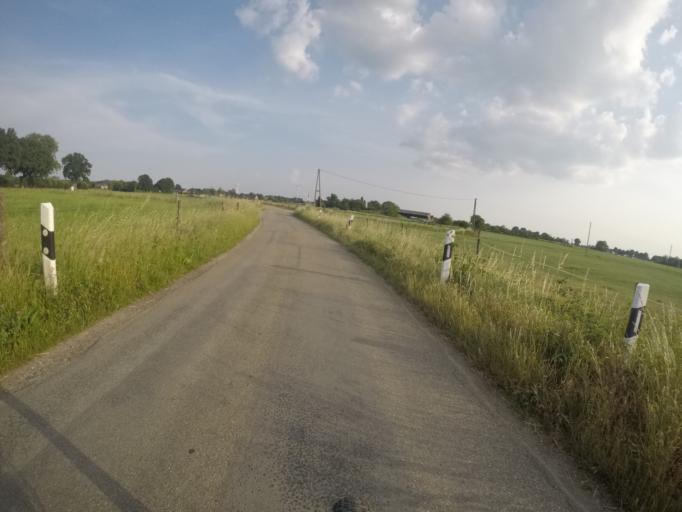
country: DE
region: North Rhine-Westphalia
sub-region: Regierungsbezirk Munster
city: Isselburg
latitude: 51.8330
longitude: 6.4151
